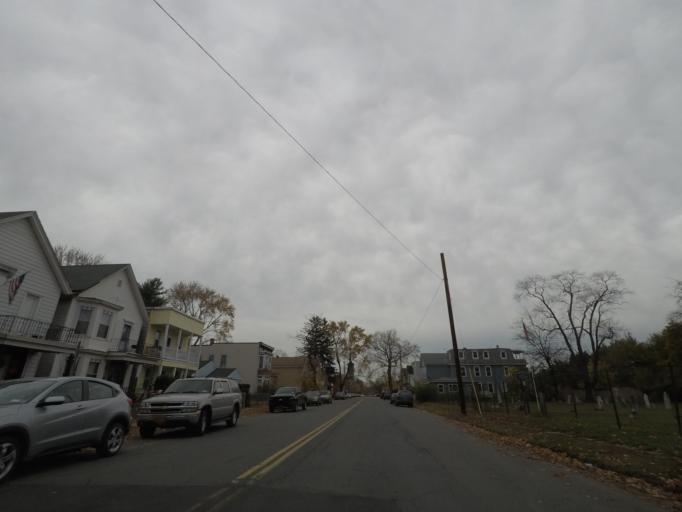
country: US
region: New York
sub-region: Albany County
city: Cohoes
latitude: 42.7646
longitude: -73.6805
